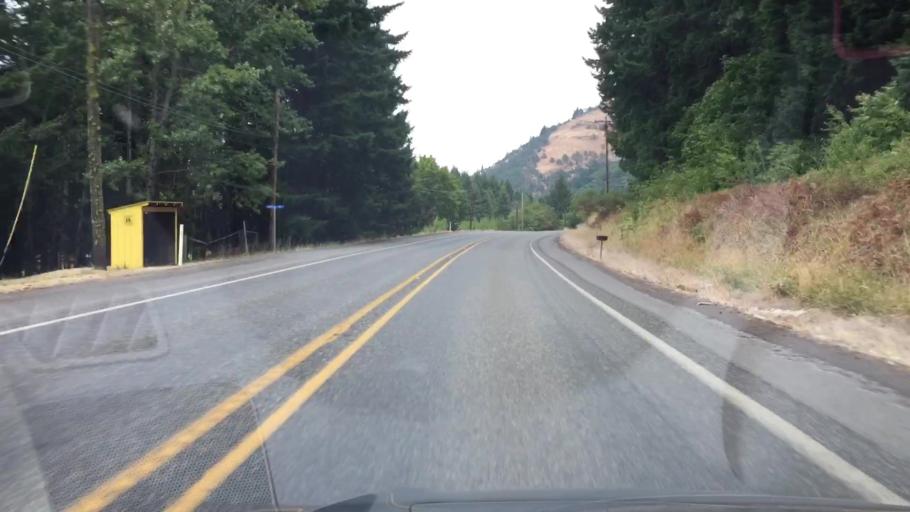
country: US
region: Washington
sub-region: Klickitat County
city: White Salmon
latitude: 45.7723
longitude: -121.5222
